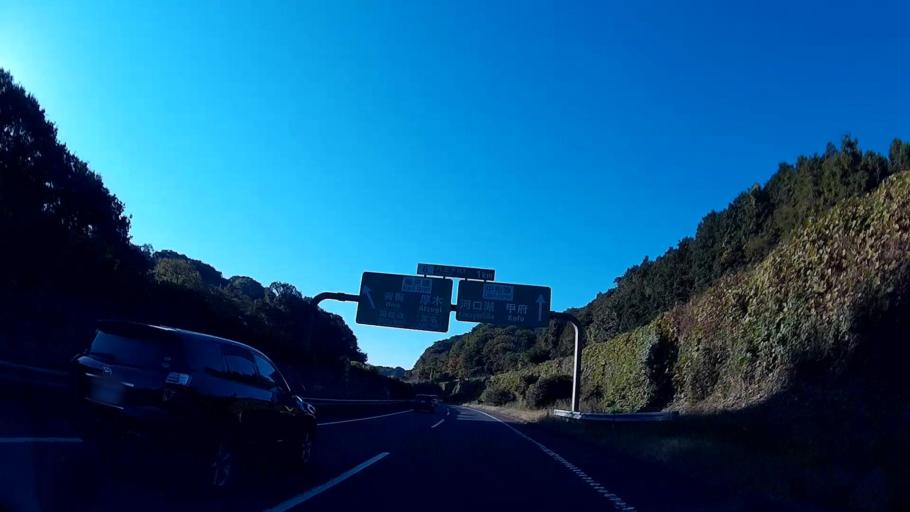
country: JP
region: Tokyo
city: Hachioji
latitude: 35.6498
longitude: 139.2657
